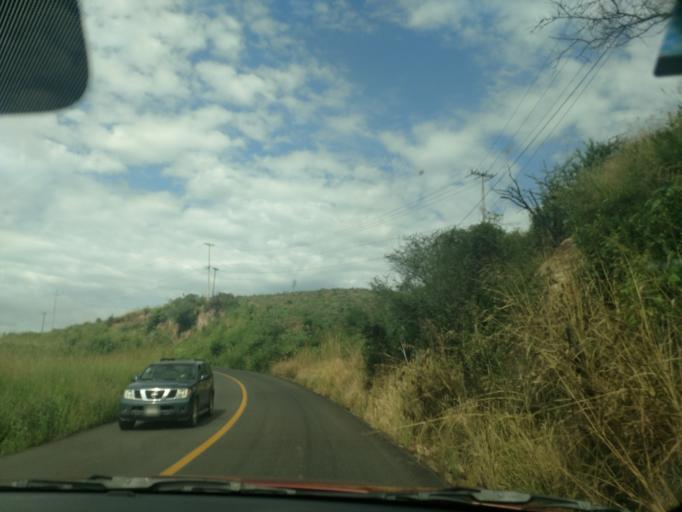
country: MX
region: Jalisco
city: El Salto
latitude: 20.4333
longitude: -104.4855
